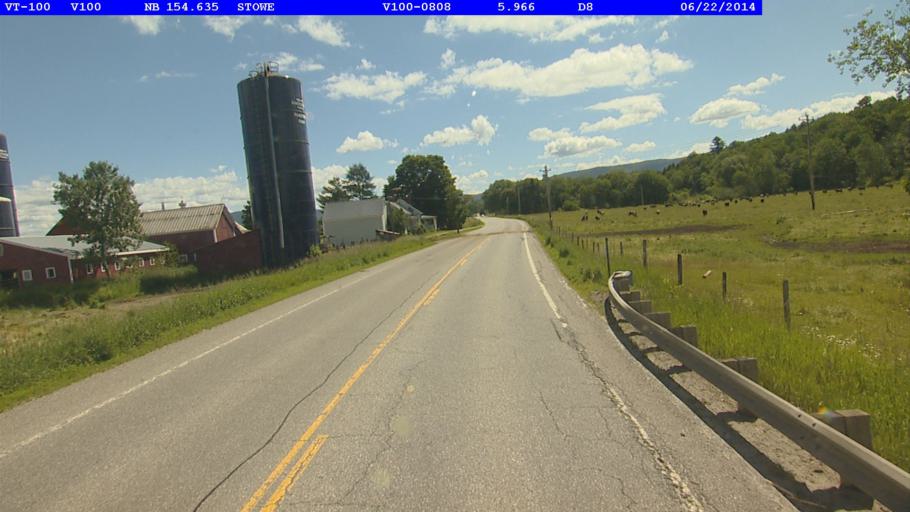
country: US
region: Vermont
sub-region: Lamoille County
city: Morristown
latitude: 44.4892
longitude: -72.6492
